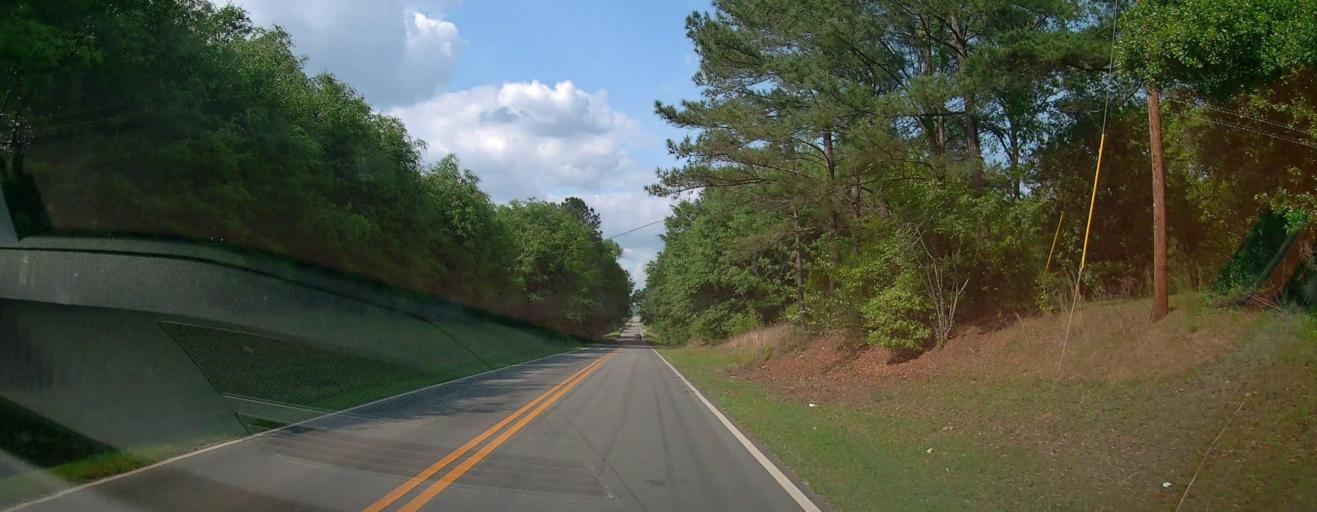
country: US
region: Georgia
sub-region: Laurens County
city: East Dublin
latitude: 32.5670
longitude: -82.8653
